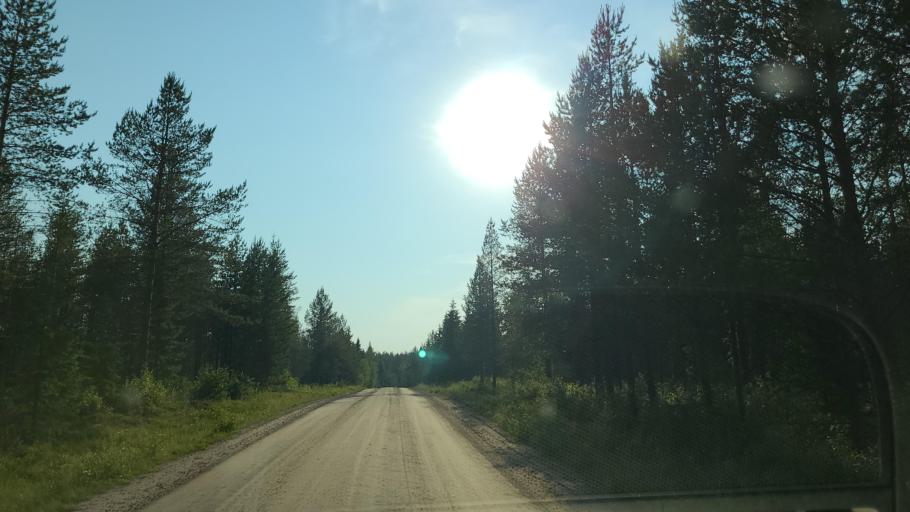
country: SE
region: Vaesterbotten
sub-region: Skelleftea Kommun
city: Burea
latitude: 64.3604
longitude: 21.4209
